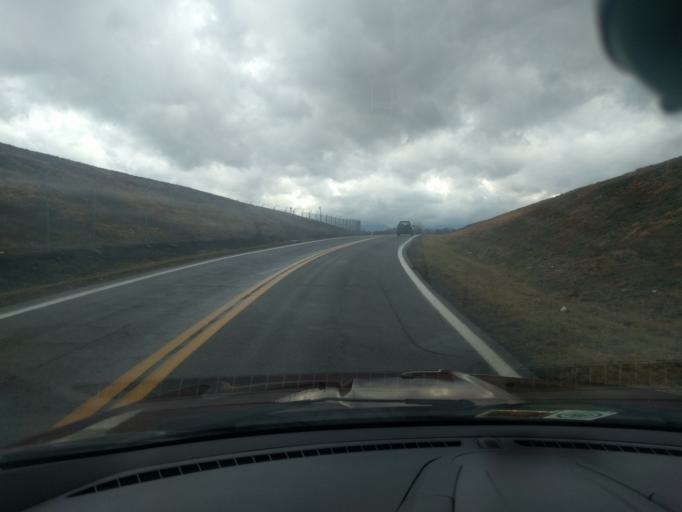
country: US
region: Virginia
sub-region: Roanoke County
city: Hollins
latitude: 37.3242
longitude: -79.9847
